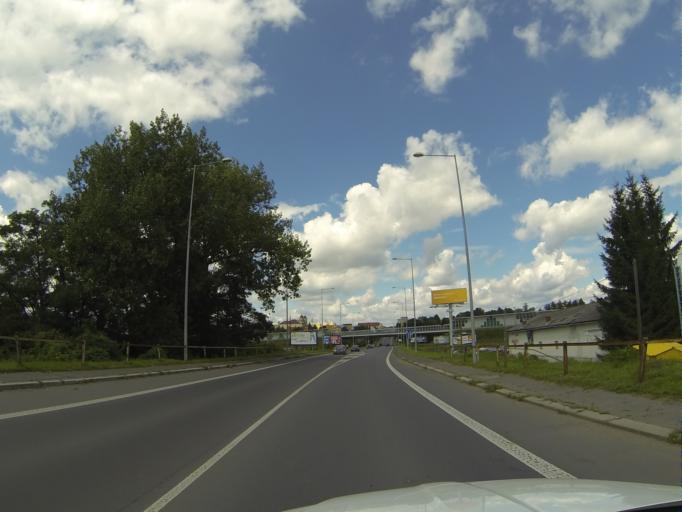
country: SK
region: Banskobystricky
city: Ziar nad Hronom
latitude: 48.5815
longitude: 18.8671
